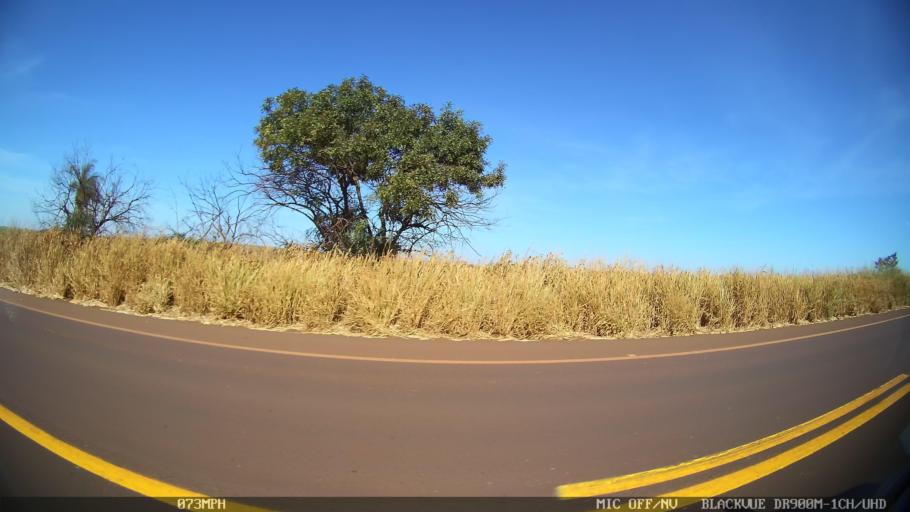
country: BR
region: Sao Paulo
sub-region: Barretos
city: Barretos
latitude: -20.4623
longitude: -48.4696
